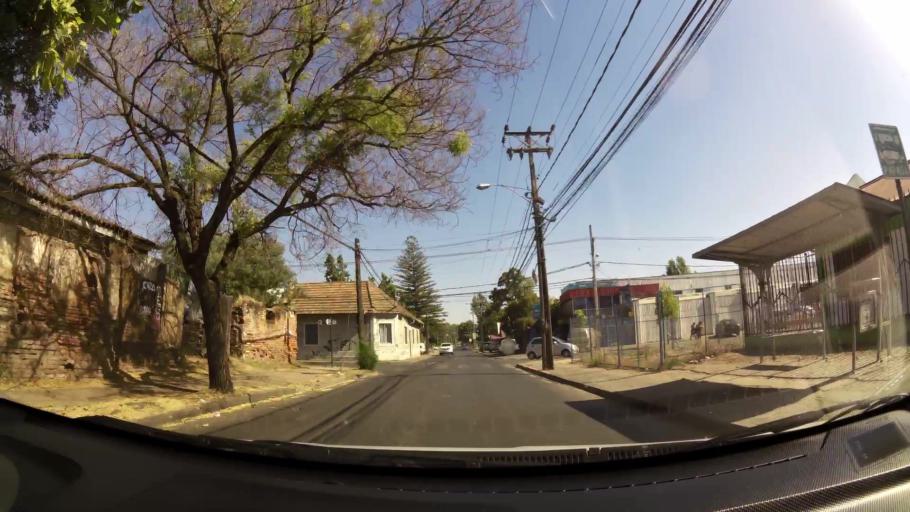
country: CL
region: Maule
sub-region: Provincia de Talca
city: Talca
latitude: -35.4325
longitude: -71.6658
